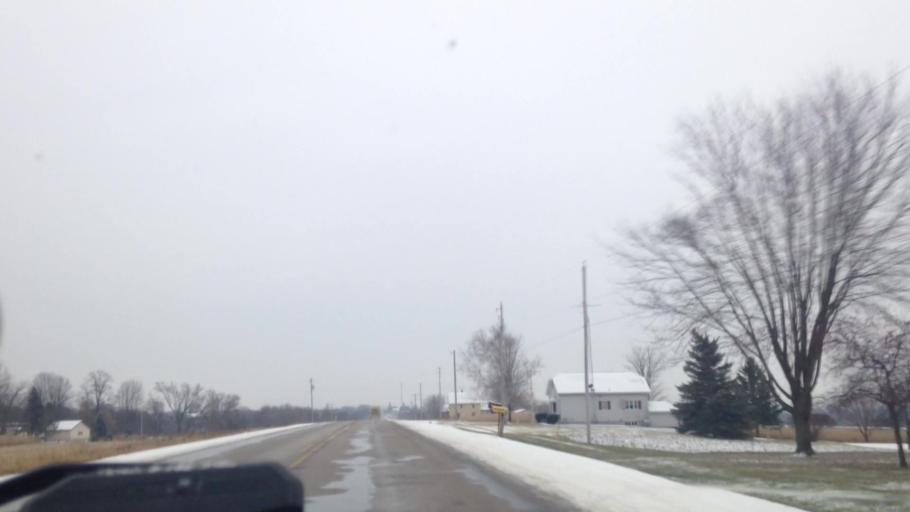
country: US
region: Wisconsin
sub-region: Dodge County
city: Mayville
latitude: 43.4166
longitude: -88.5421
